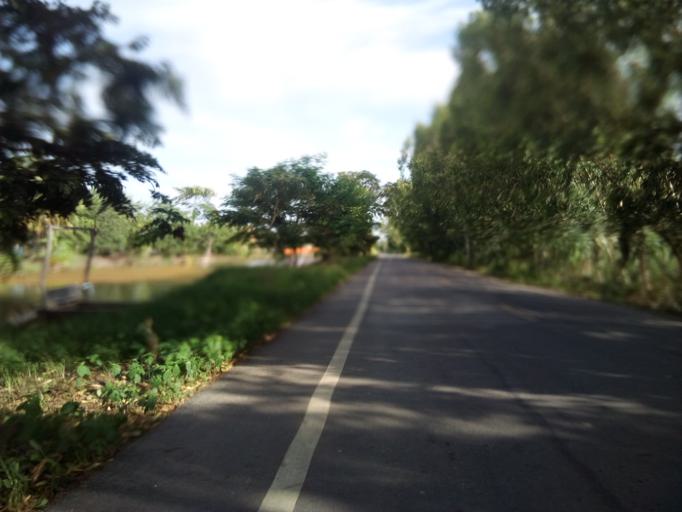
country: TH
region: Pathum Thani
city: Nong Suea
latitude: 14.1165
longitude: 100.8460
